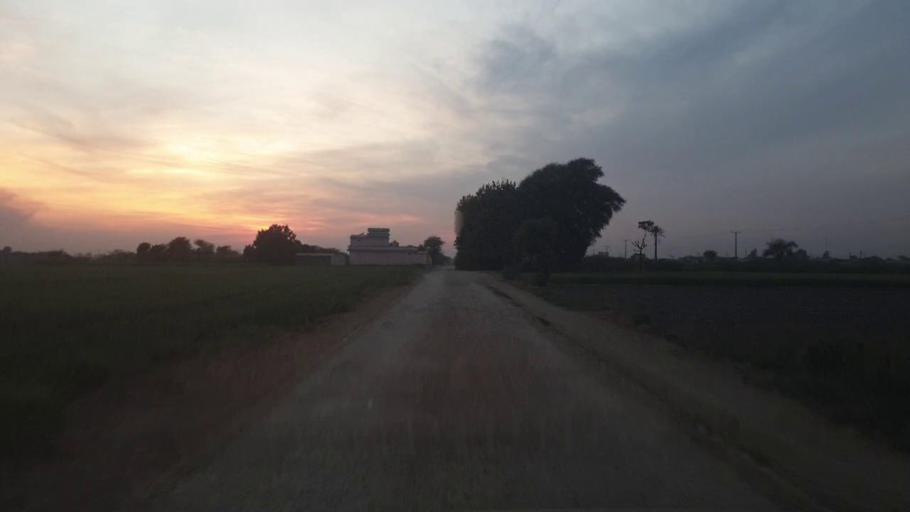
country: PK
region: Sindh
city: Kunri
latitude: 25.2241
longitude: 69.5283
